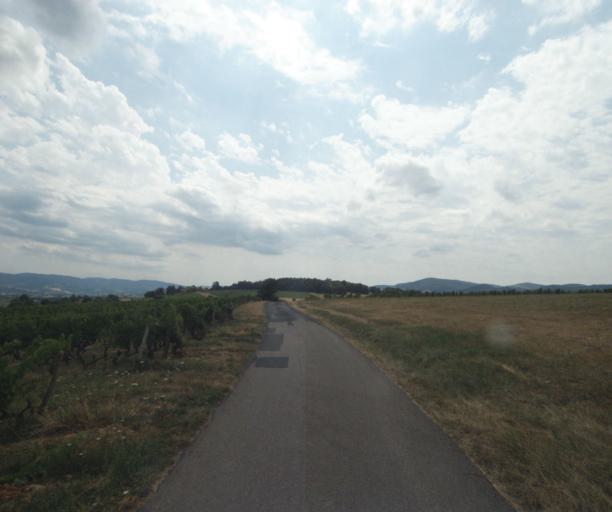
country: FR
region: Rhone-Alpes
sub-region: Departement du Rhone
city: Bully
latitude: 45.8639
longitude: 4.5890
